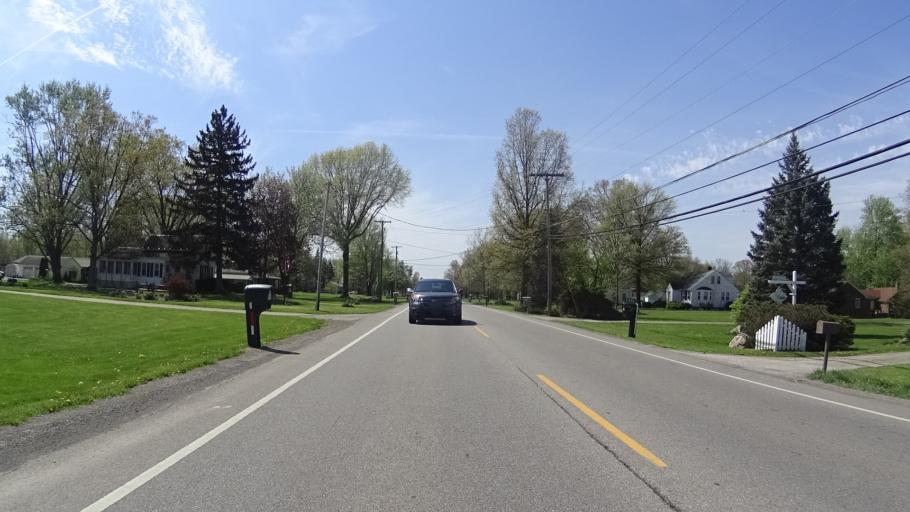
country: US
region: Ohio
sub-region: Lorain County
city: Elyria
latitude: 41.3284
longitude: -82.1175
